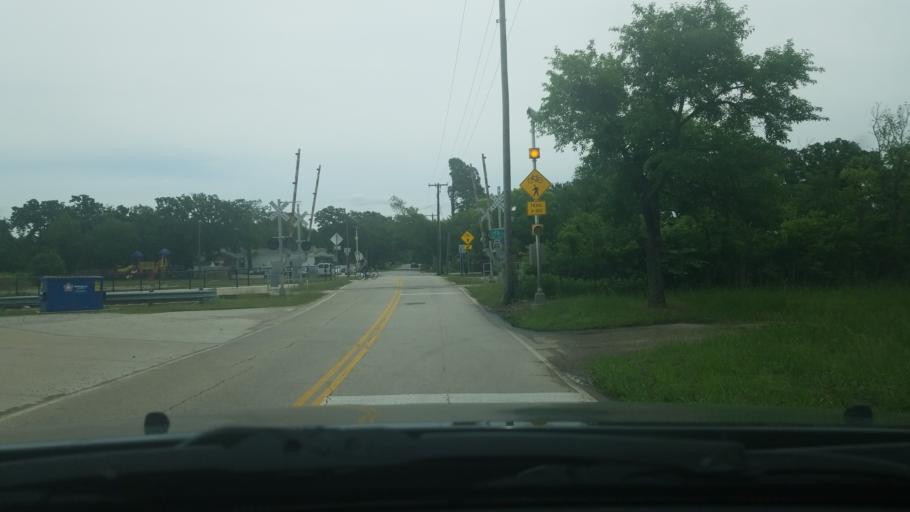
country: US
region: Texas
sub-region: Denton County
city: Lake Dallas
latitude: 33.1150
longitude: -97.0269
